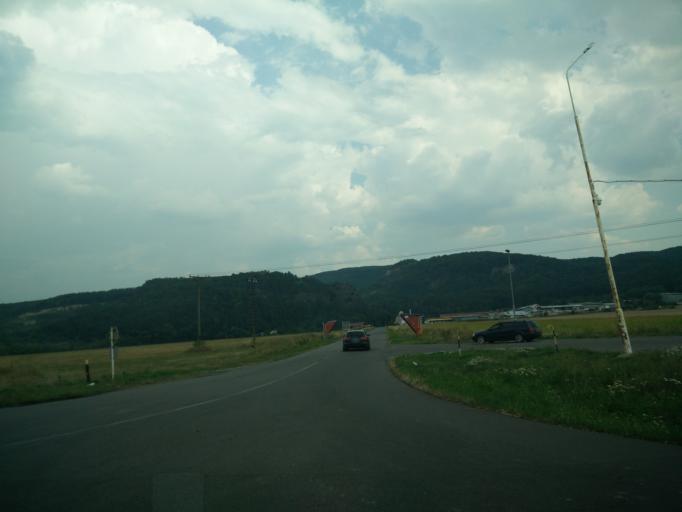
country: SK
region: Banskobystricky
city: Ziar nad Hronom
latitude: 48.5408
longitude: 18.7929
